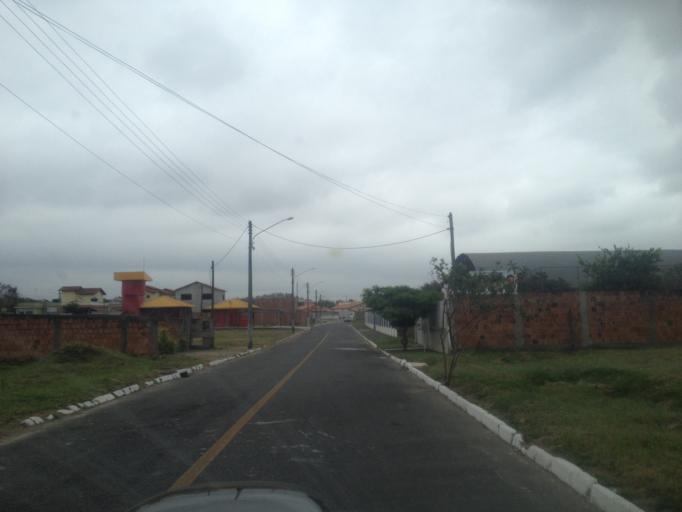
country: BR
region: Rio de Janeiro
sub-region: Porto Real
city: Porto Real
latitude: -22.4119
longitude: -44.3093
